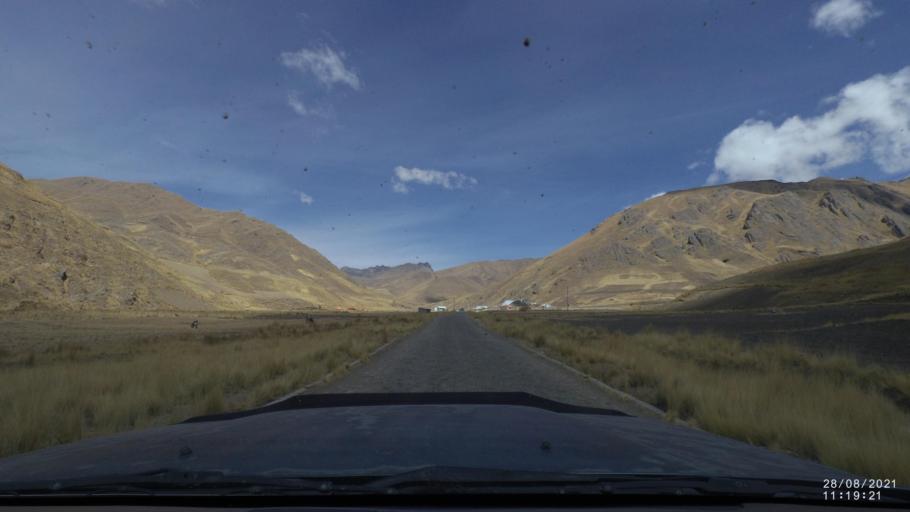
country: BO
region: Cochabamba
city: Cochabamba
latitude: -17.1531
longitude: -66.3315
